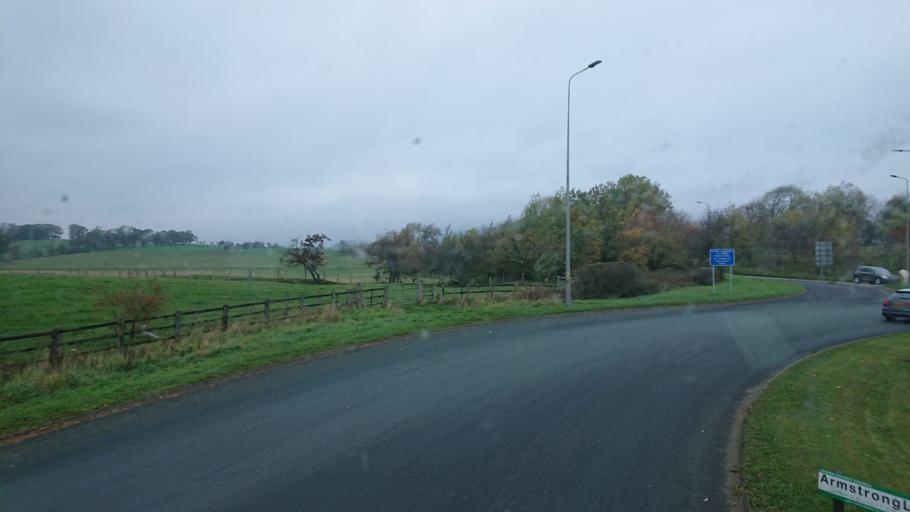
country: GB
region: England
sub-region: North Yorkshire
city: Skipton
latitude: 53.9710
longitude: -2.0274
